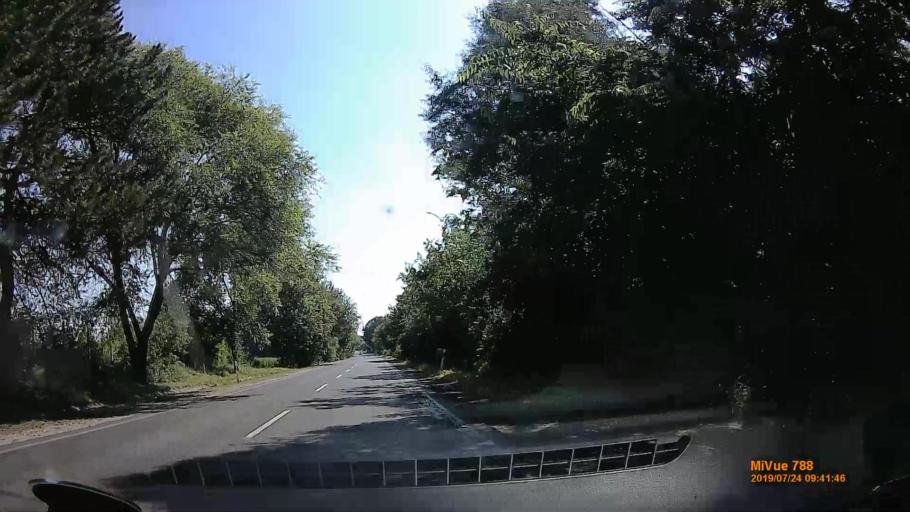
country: HU
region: Szabolcs-Szatmar-Bereg
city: Levelek
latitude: 47.9705
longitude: 21.9972
